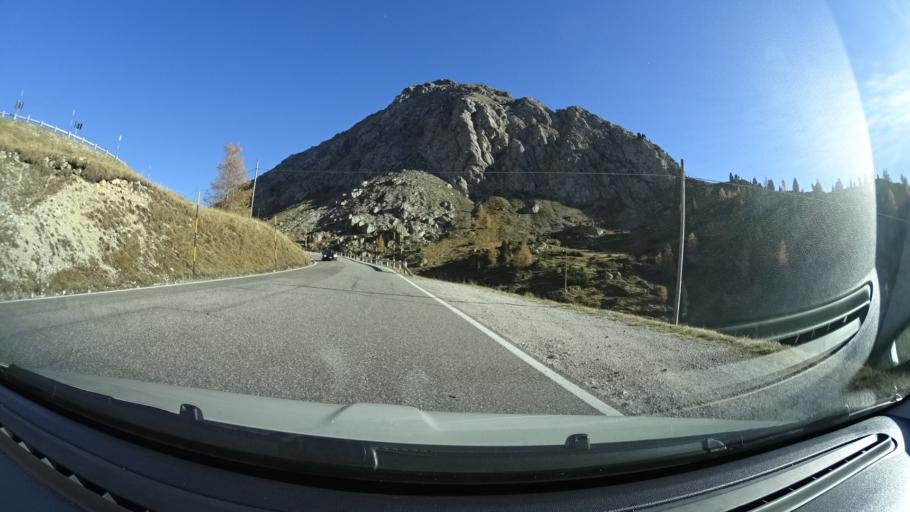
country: IT
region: Trentino-Alto Adige
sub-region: Provincia di Trento
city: Canazei
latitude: 46.4888
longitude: 11.8045
